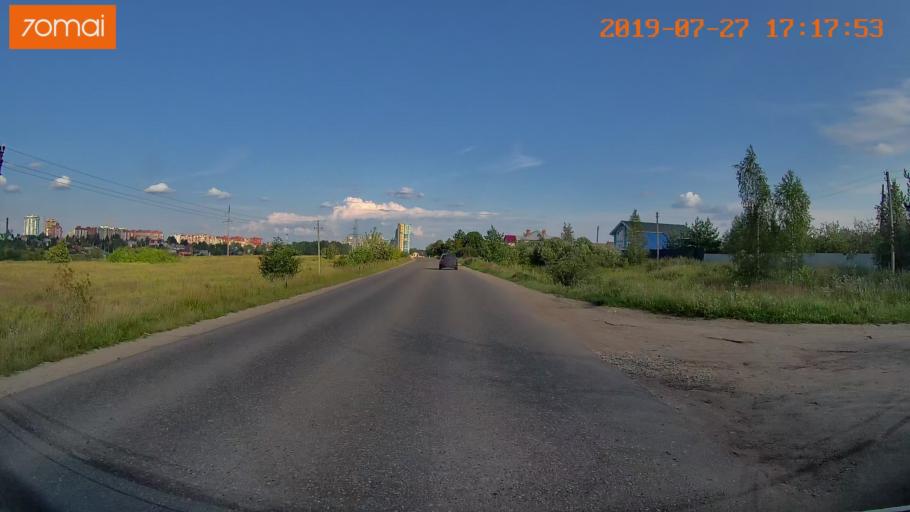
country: RU
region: Ivanovo
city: Novo-Talitsy
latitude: 57.0337
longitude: 40.8998
